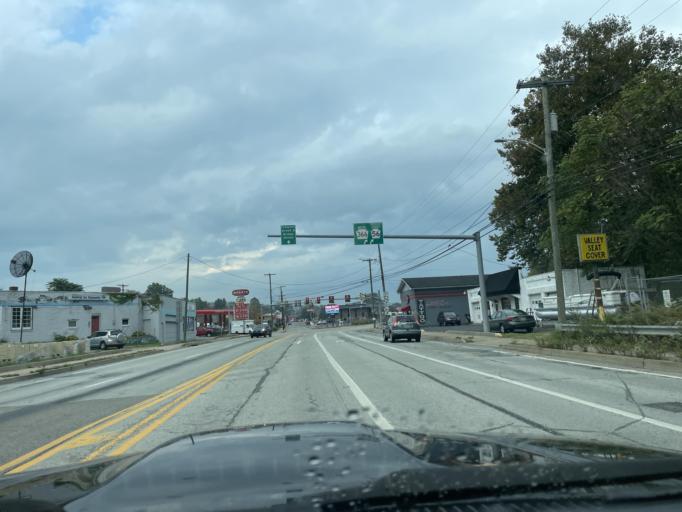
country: US
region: Pennsylvania
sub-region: Westmoreland County
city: Lower Burrell
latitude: 40.5542
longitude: -79.7581
